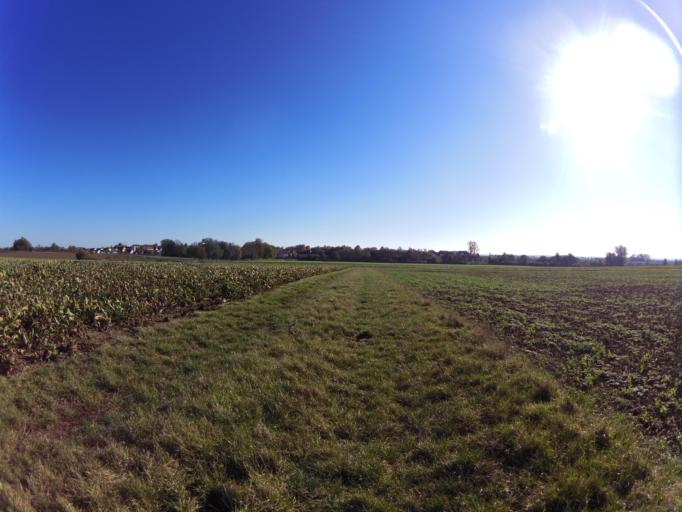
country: DE
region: Bavaria
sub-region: Regierungsbezirk Unterfranken
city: Giebelstadt
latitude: 49.6604
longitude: 9.9349
